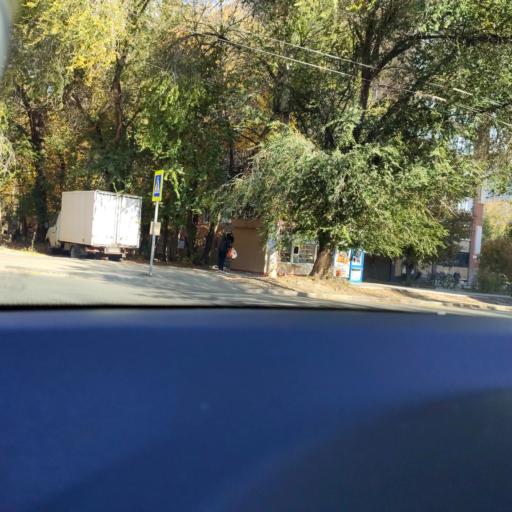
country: RU
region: Samara
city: Petra-Dubrava
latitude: 53.2502
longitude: 50.2577
